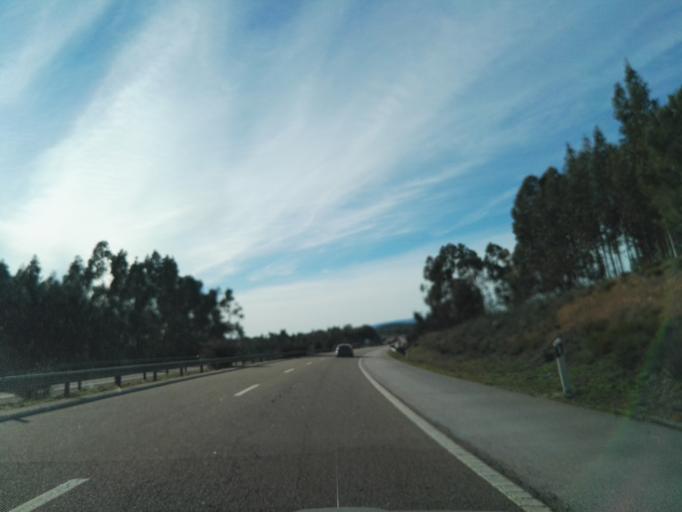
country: PT
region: Santarem
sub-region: Constancia
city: Constancia
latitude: 39.4848
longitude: -8.3717
